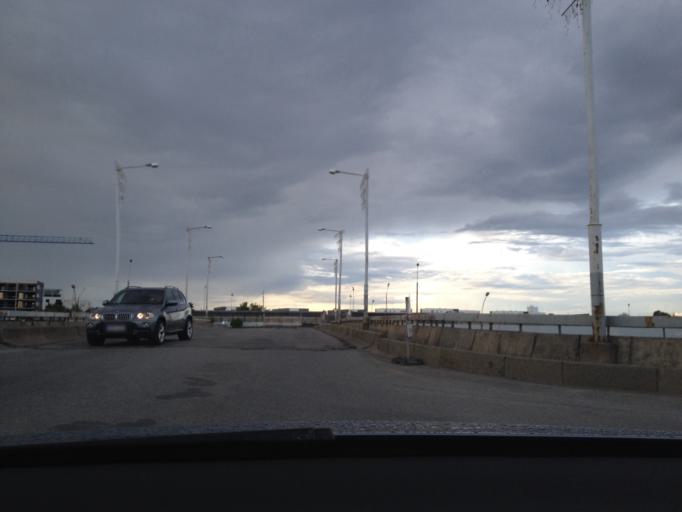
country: EE
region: Harju
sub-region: Tallinna linn
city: Tallinn
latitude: 59.4363
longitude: 24.8111
